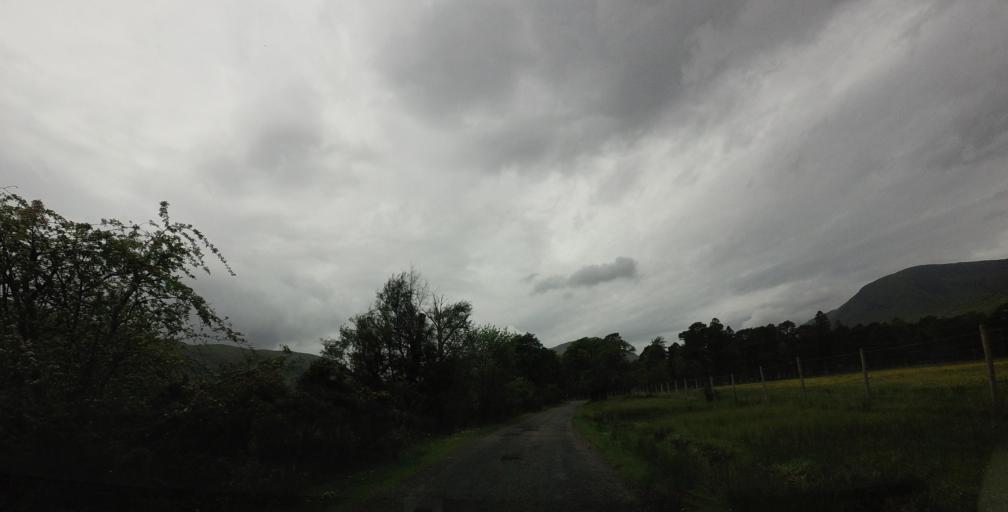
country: GB
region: Scotland
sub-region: Highland
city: Fort William
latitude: 56.7671
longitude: -5.2338
